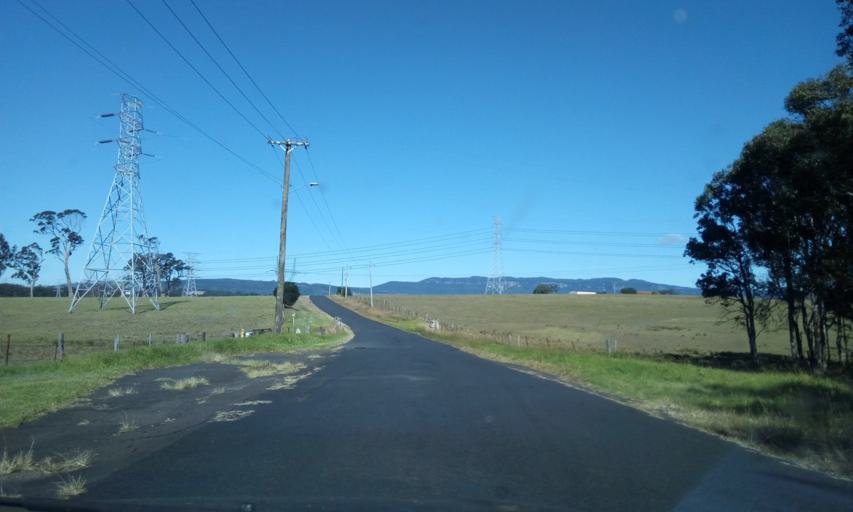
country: AU
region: New South Wales
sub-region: Wollongong
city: Dapto
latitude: -34.5211
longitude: 150.7793
